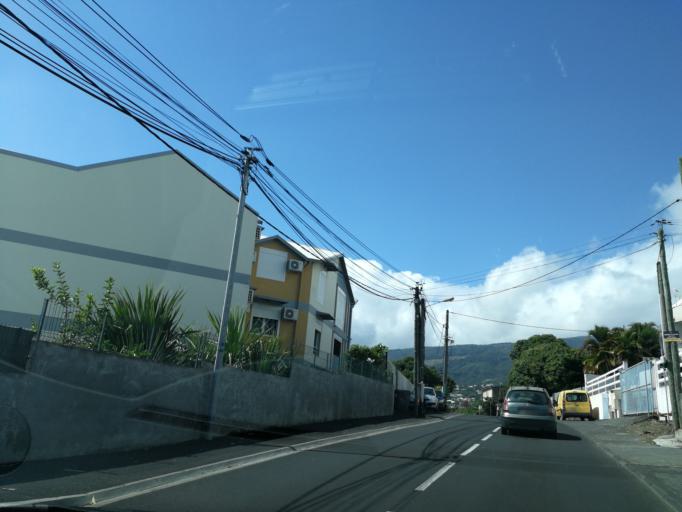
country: RE
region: Reunion
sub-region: Reunion
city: Saint-Denis
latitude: -20.9113
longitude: 55.4818
